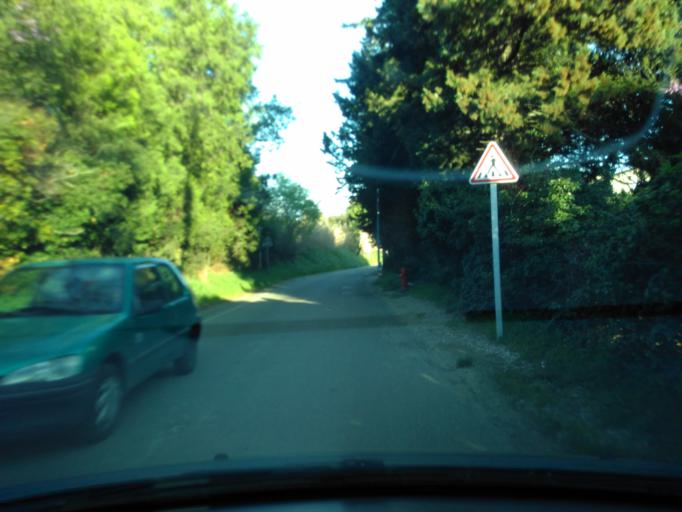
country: FR
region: Provence-Alpes-Cote d'Azur
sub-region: Departement du Vaucluse
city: Carpentras
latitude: 44.0527
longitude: 5.0599
